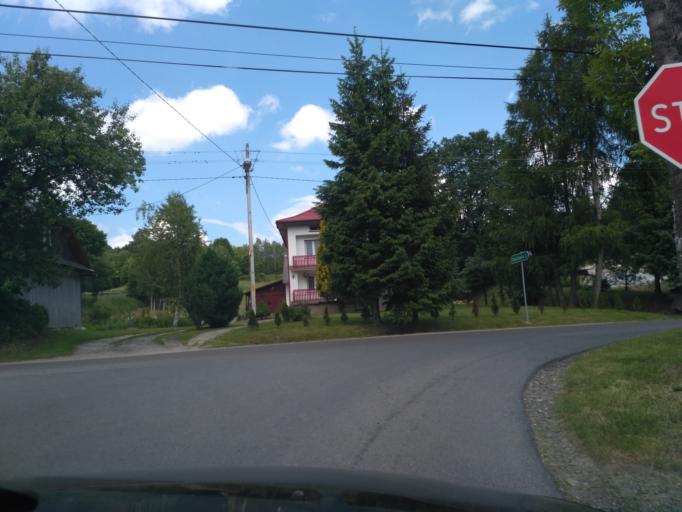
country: PL
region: Subcarpathian Voivodeship
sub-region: Powiat rzeszowski
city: Blazowa
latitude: 49.8740
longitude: 22.0672
